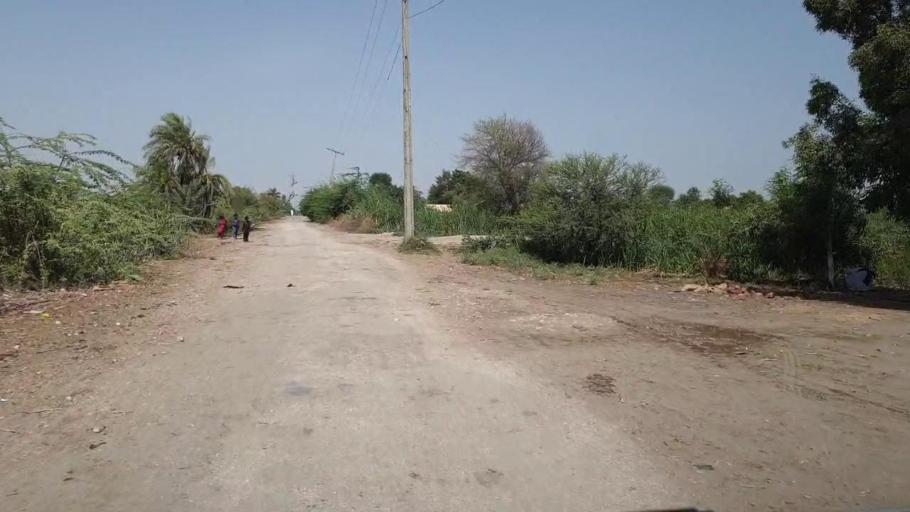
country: PK
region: Sindh
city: Jam Sahib
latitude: 26.4065
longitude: 68.8770
